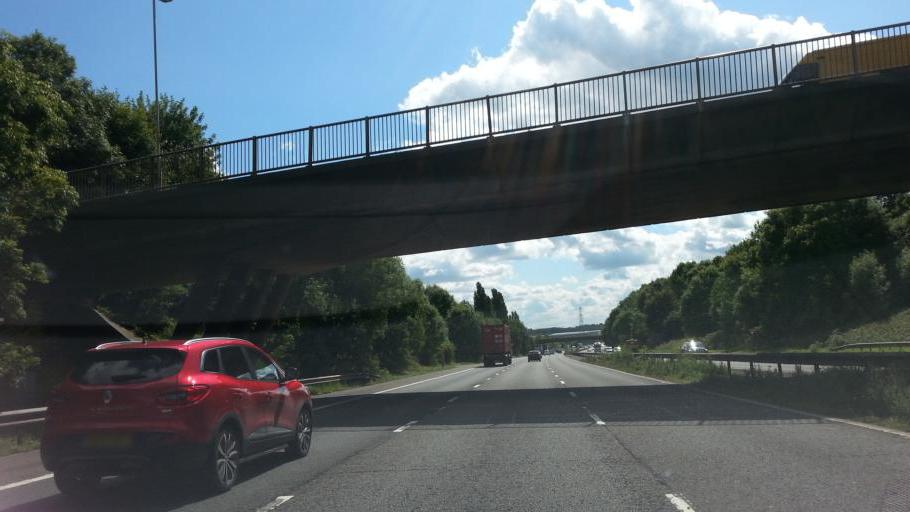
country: GB
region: England
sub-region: Leicestershire
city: Kirby Muxloe
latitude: 52.6526
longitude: -1.2391
